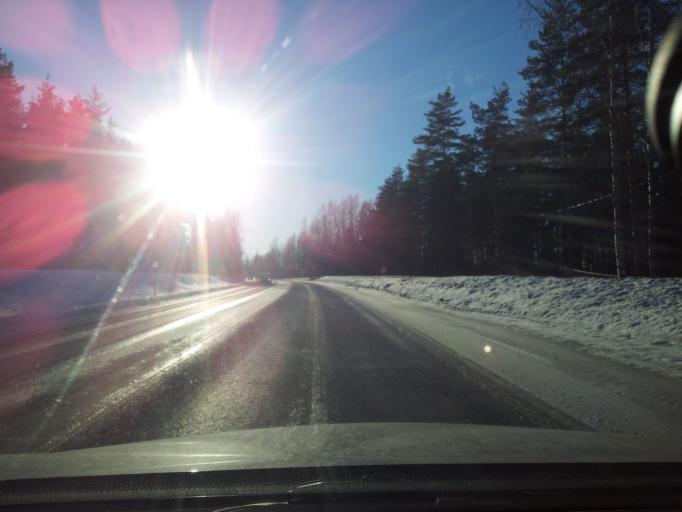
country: FI
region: Uusimaa
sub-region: Helsinki
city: Vihti
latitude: 60.3579
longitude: 24.3410
